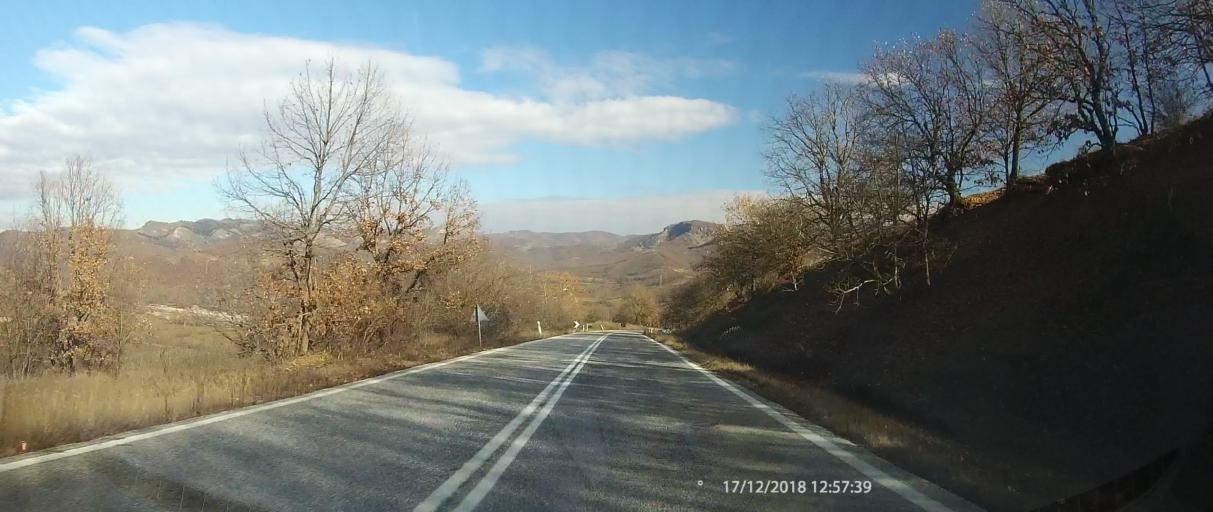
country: GR
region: Thessaly
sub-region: Trikala
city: Kastraki
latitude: 39.7438
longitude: 21.5334
